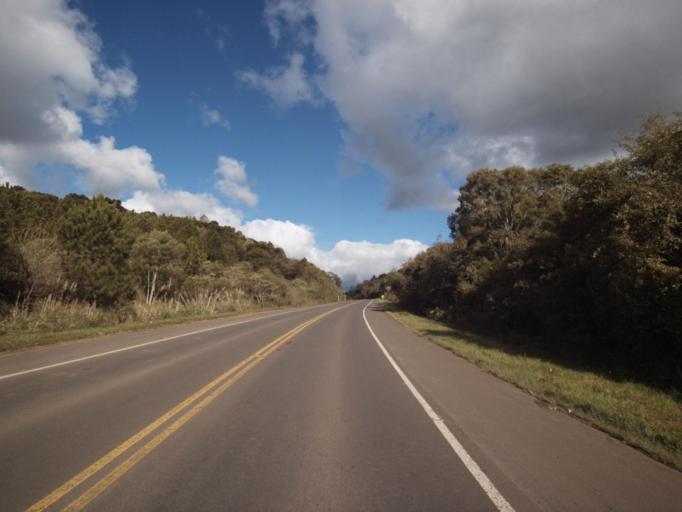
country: BR
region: Santa Catarina
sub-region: Joacaba
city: Joacaba
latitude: -27.0321
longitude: -51.7219
